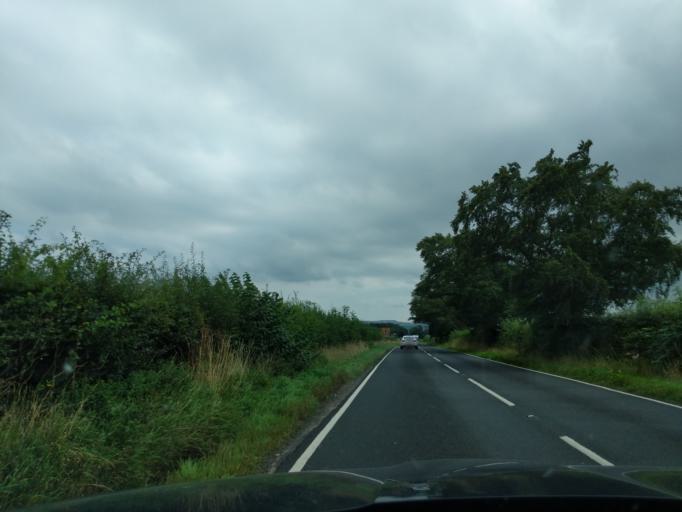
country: GB
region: England
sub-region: Northumberland
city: Whittingham
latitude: 55.4265
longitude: -1.8794
